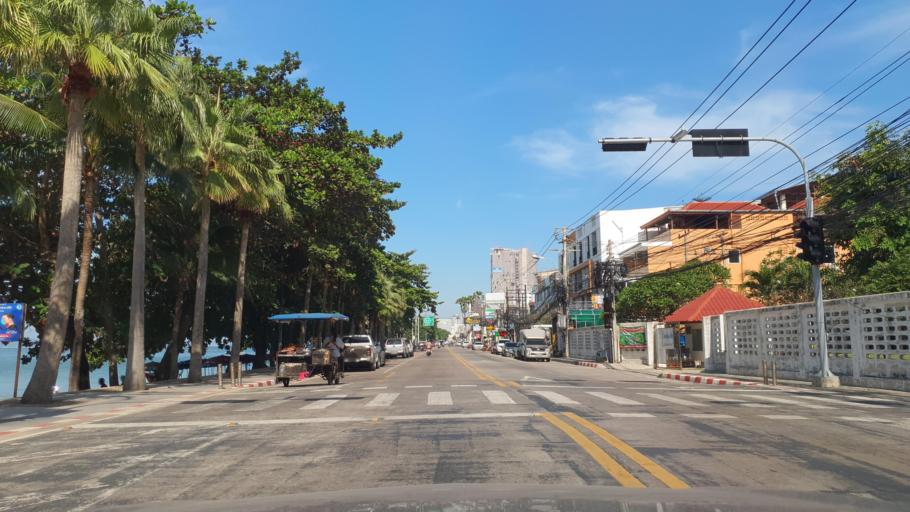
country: TH
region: Chon Buri
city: Phatthaya
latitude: 12.8809
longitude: 100.8823
